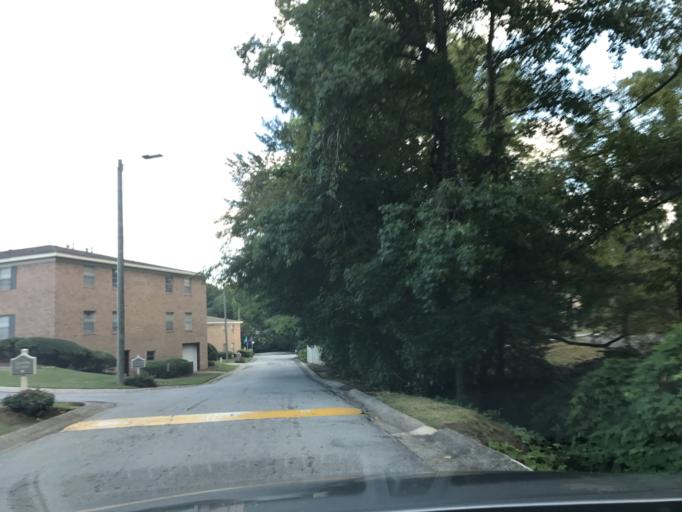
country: US
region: Georgia
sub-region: Douglas County
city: Douglasville
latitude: 33.7489
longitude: -84.7299
